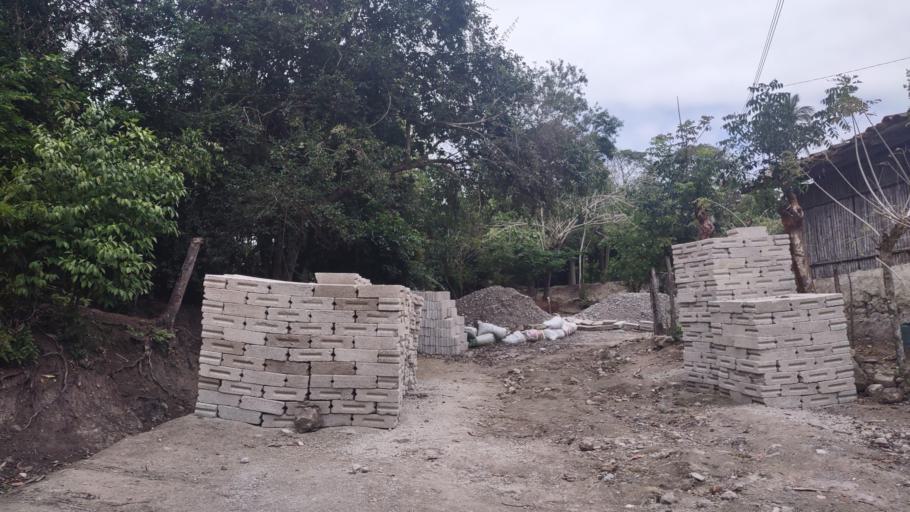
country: MX
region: Veracruz
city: Papantla de Olarte
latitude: 20.4362
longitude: -97.2651
